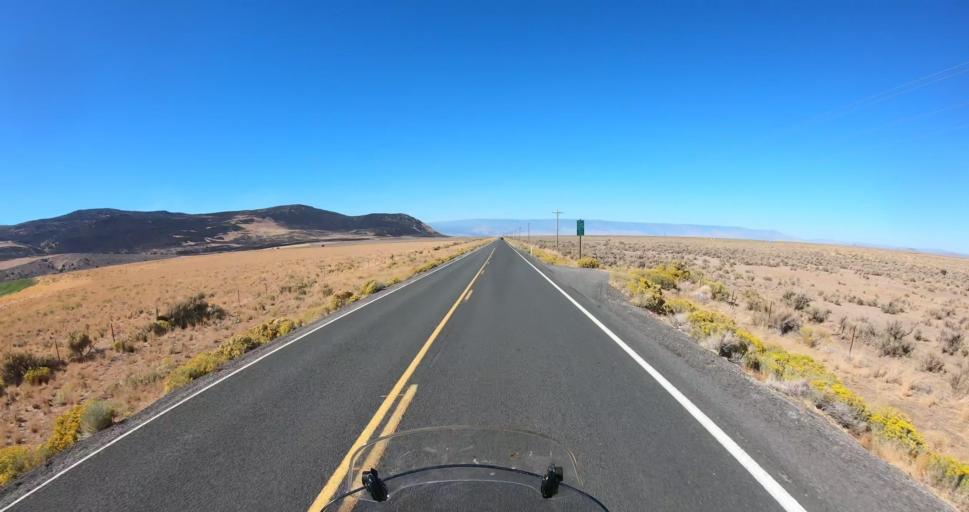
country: US
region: Oregon
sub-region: Lake County
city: Lakeview
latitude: 42.7068
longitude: -120.5534
